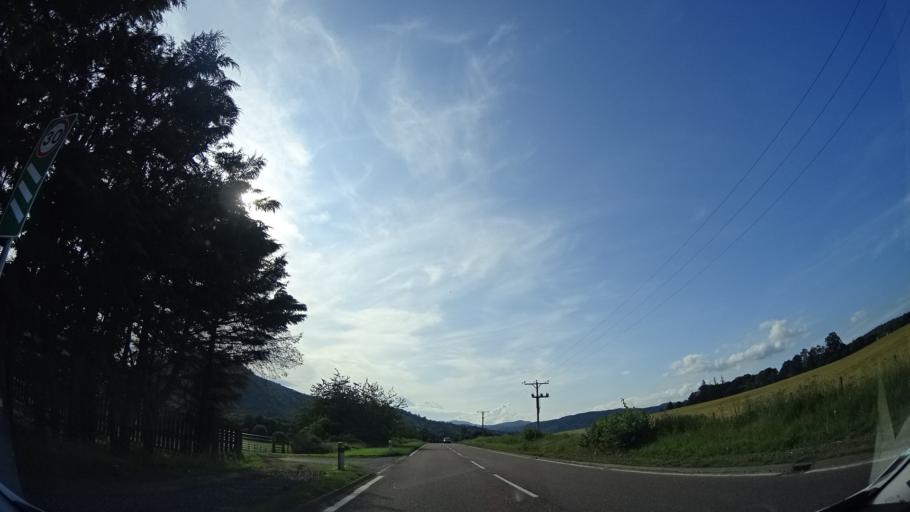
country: GB
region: Scotland
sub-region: Highland
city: Muir of Ord
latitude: 57.5623
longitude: -4.5701
